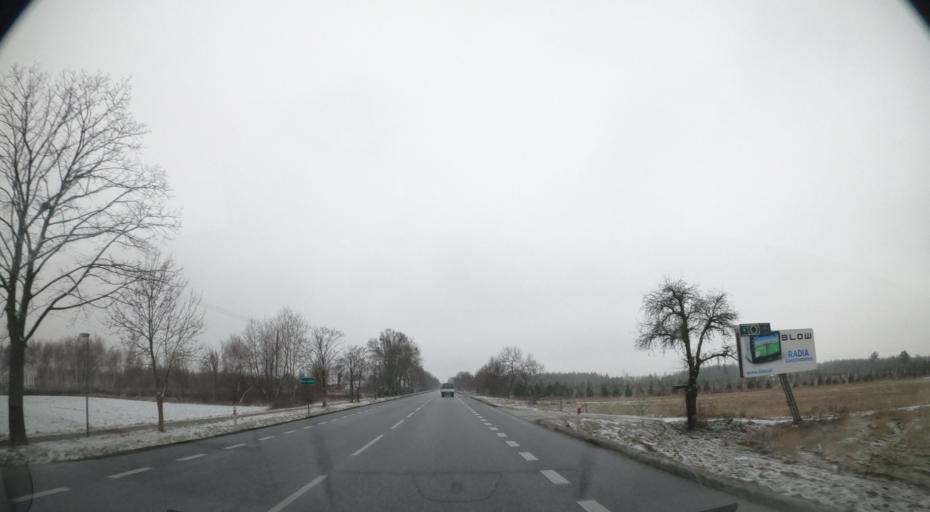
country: PL
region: Masovian Voivodeship
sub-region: Powiat warszawski zachodni
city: Bieniewice
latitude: 52.2011
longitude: 20.5551
